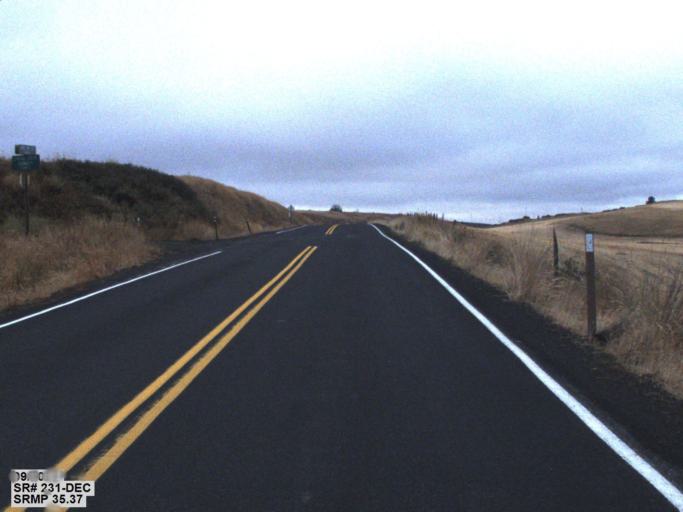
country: US
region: Washington
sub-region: Spokane County
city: Medical Lake
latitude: 47.7301
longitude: -117.8703
